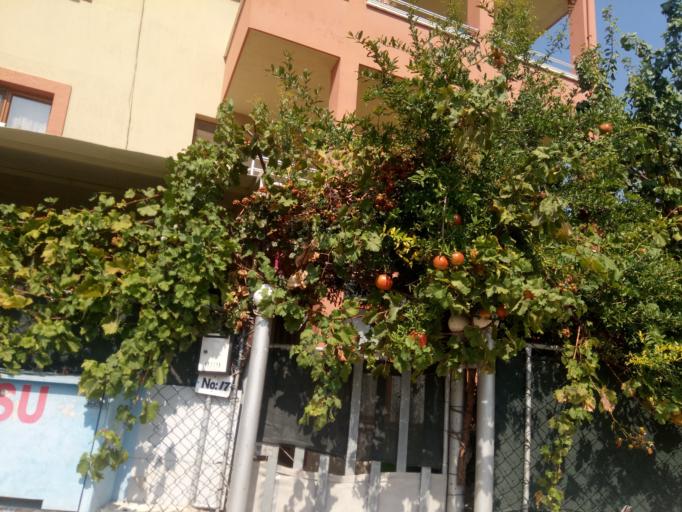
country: TR
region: Izmir
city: Urla
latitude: 38.3252
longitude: 26.7703
